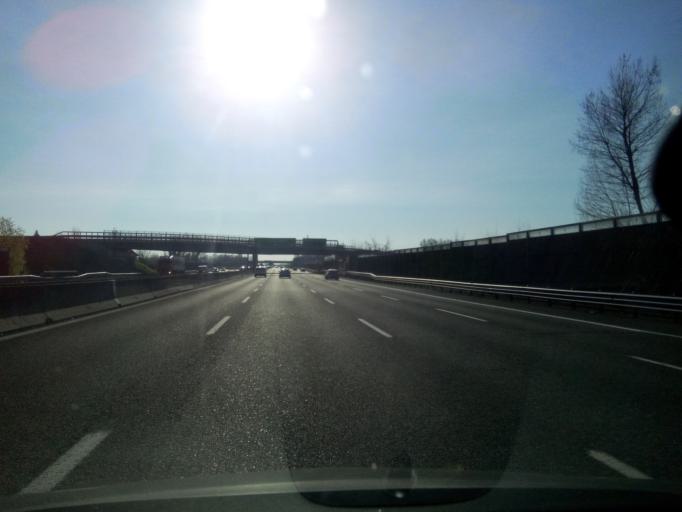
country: IT
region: Emilia-Romagna
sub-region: Provincia di Modena
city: San Damaso
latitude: 44.5802
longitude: 10.9759
